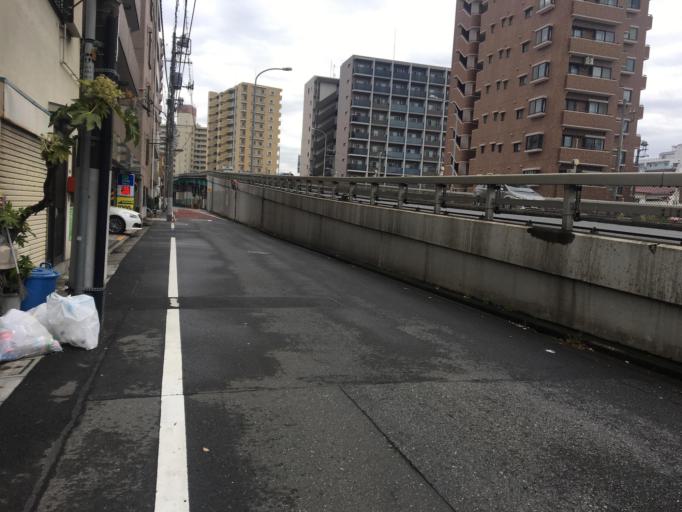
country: JP
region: Tokyo
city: Urayasu
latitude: 35.7018
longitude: 139.8315
